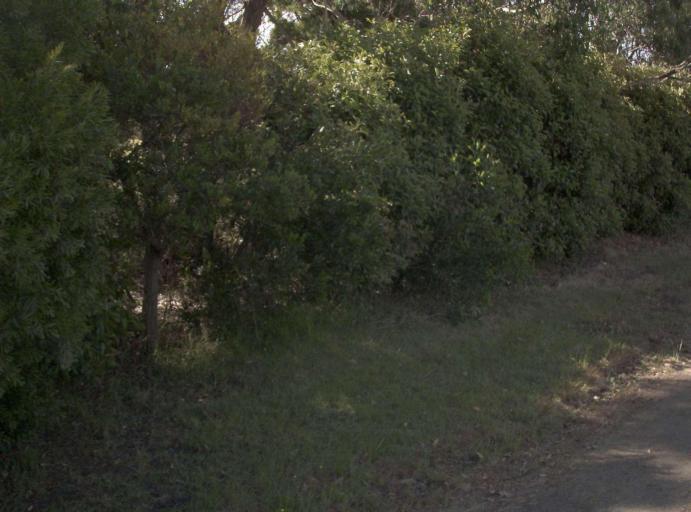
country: AU
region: Victoria
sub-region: Latrobe
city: Morwell
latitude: -38.2241
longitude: 146.3969
